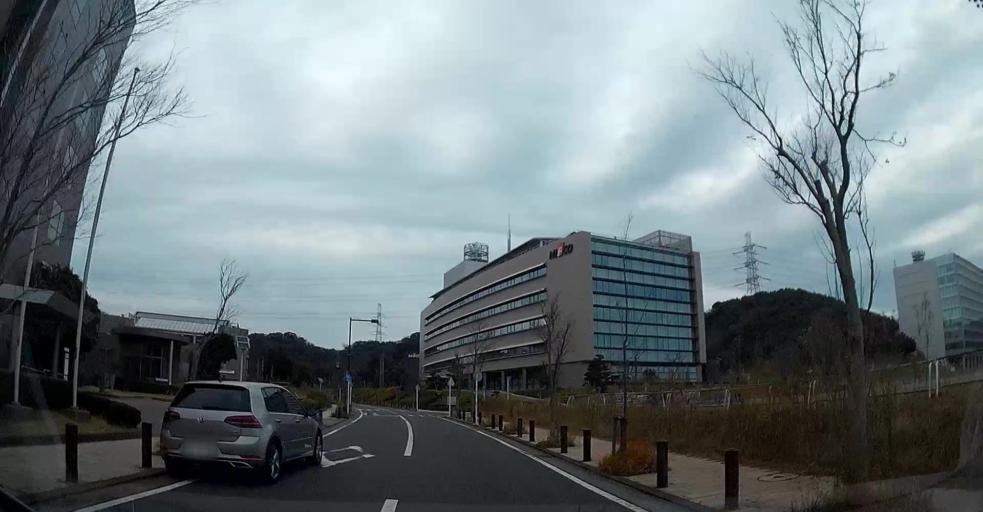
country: JP
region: Kanagawa
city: Yokosuka
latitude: 35.2236
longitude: 139.6750
